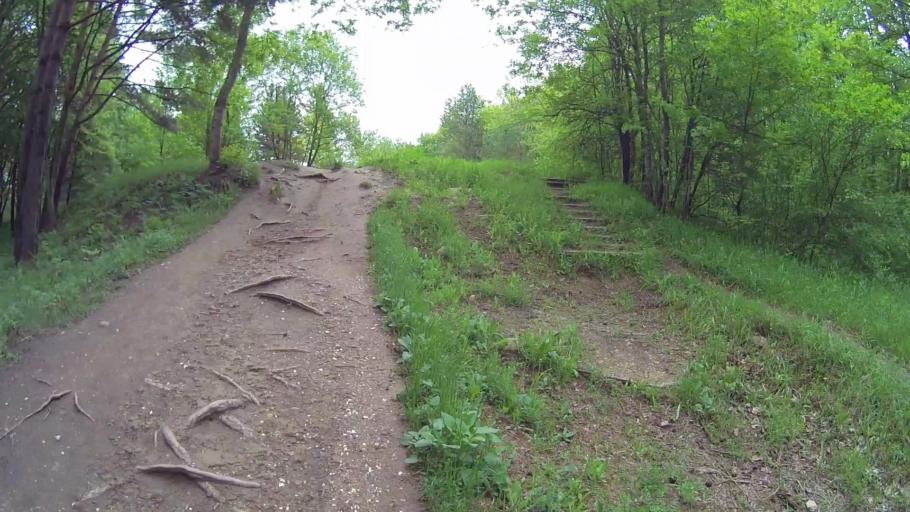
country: RU
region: Stavropol'skiy
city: Kislovodsk
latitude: 43.8943
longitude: 42.7264
